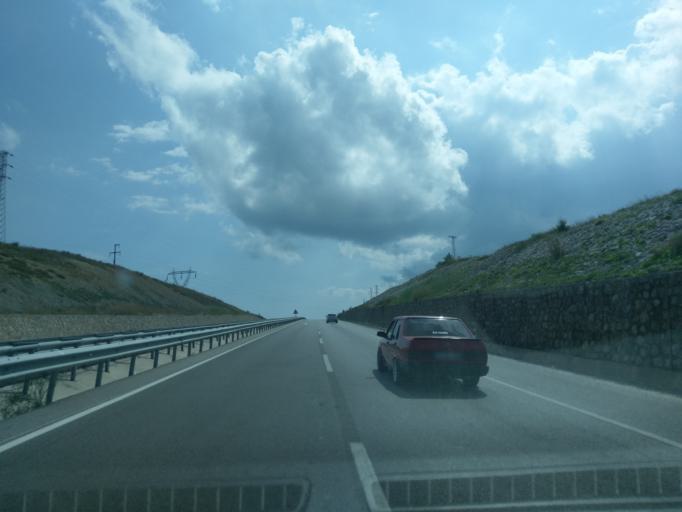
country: TR
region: Sinop
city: Kabali
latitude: 41.8545
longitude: 35.1154
